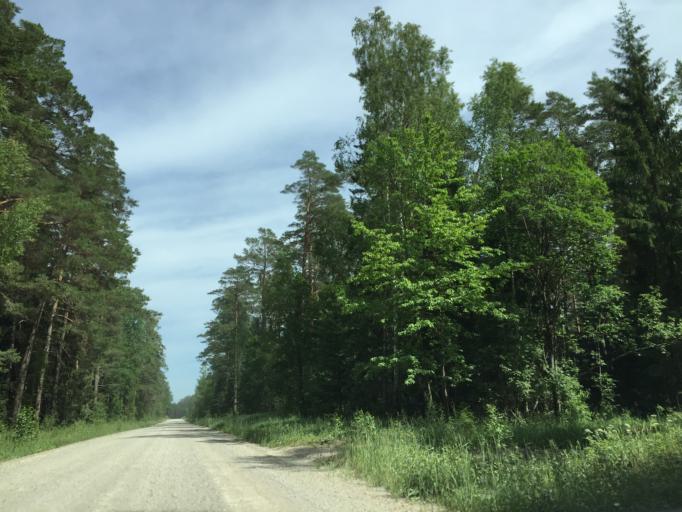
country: LV
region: Dundaga
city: Dundaga
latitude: 57.6197
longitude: 22.5443
